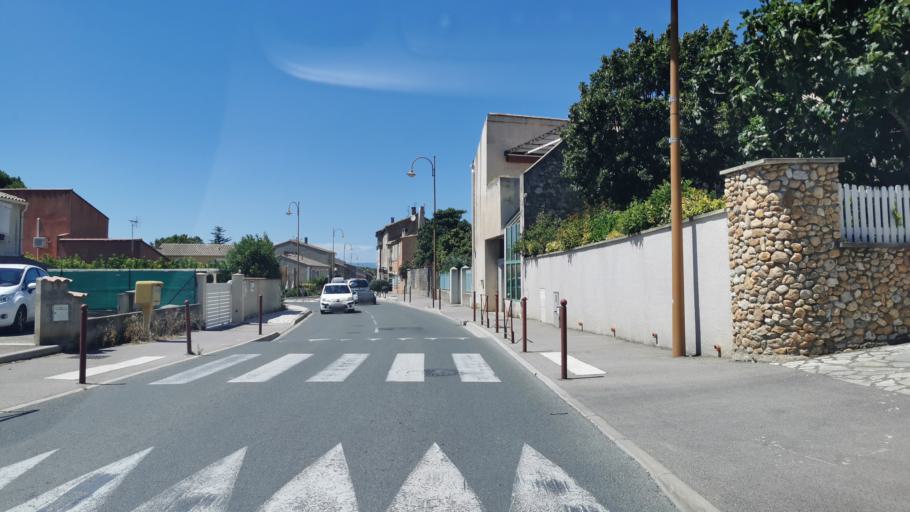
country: FR
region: Languedoc-Roussillon
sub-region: Departement de l'Aude
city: Fleury
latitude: 43.2343
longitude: 3.1223
